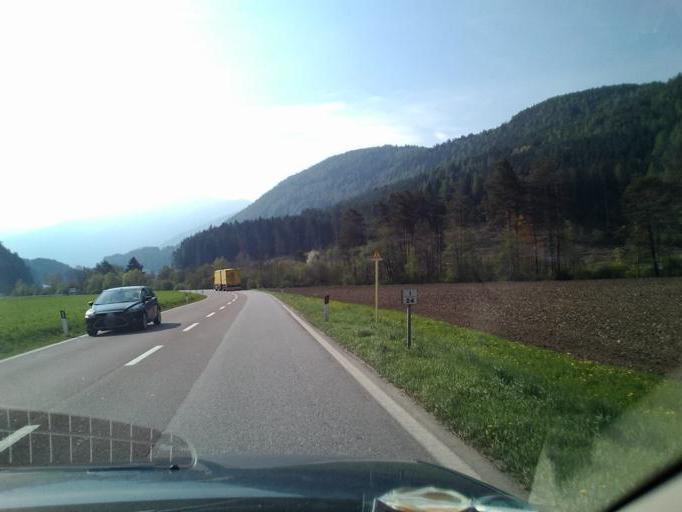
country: IT
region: Trentino-Alto Adige
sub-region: Bolzano
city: Chienes
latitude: 46.7982
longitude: 11.8504
